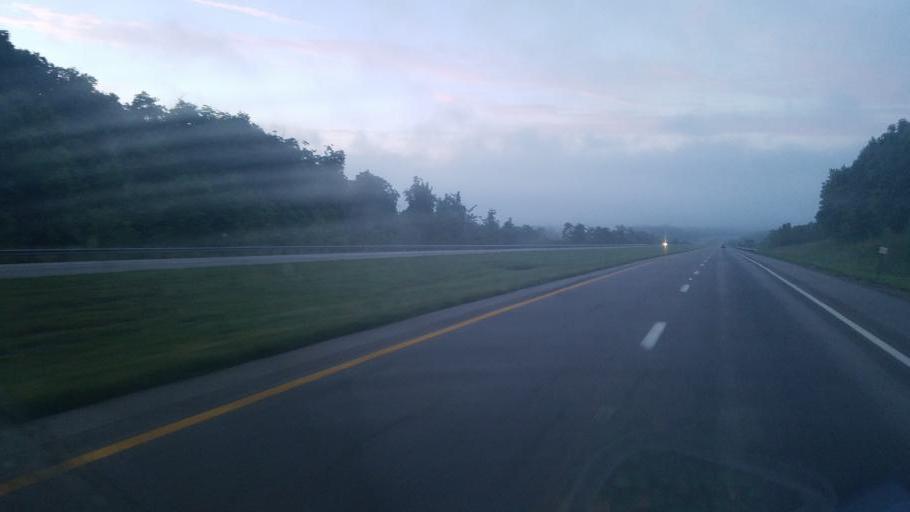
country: US
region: Ohio
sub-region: Pike County
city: Waverly
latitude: 39.2264
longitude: -82.8312
